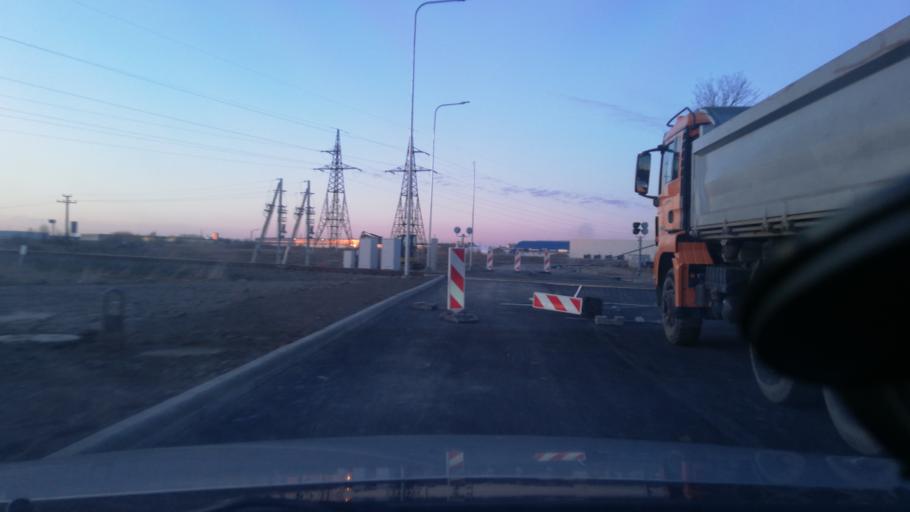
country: LT
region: Klaipedos apskritis
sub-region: Klaipeda
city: Klaipeda
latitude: 55.6831
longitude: 21.1971
